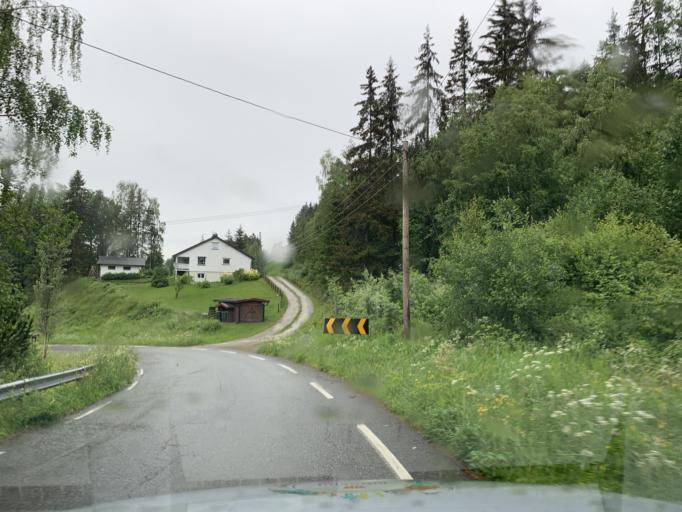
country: NO
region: Oppland
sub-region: Oyer
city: Tretten
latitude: 61.3941
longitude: 10.2404
